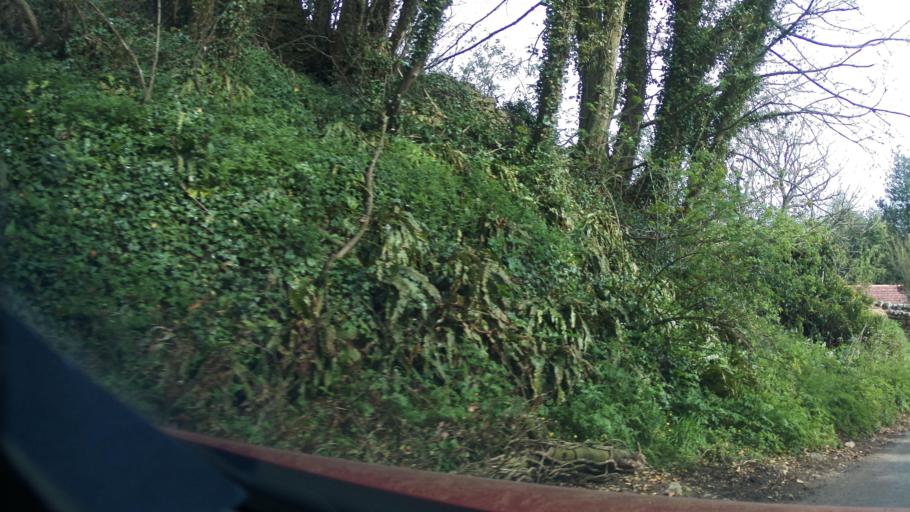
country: GB
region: England
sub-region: Somerset
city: Milborne Port
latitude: 50.9857
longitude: -2.4739
